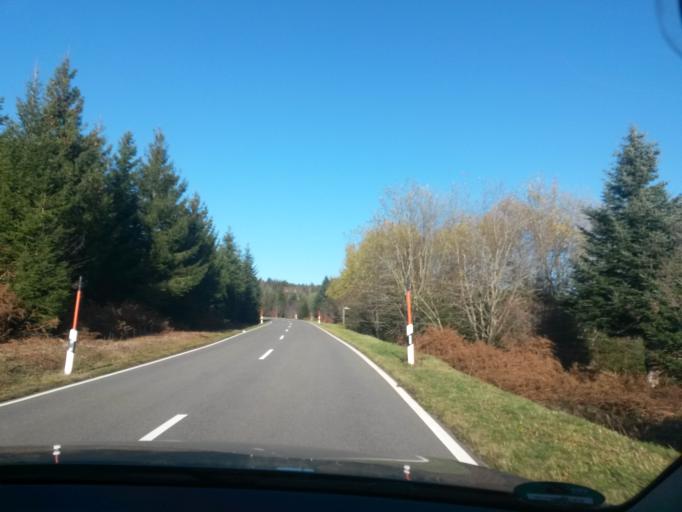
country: DE
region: Baden-Wuerttemberg
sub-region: Karlsruhe Region
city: Bad Rippoldsau-Schapbach
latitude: 48.4617
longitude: 8.2991
